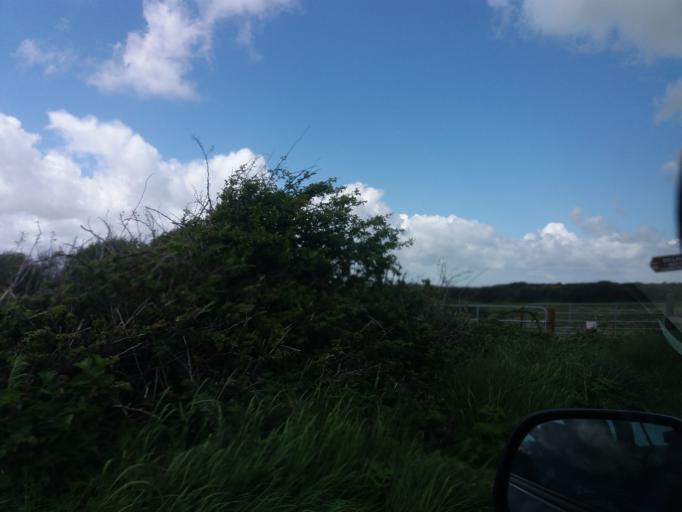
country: IE
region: Munster
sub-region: Waterford
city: Dunmore East
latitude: 52.1973
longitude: -6.8996
